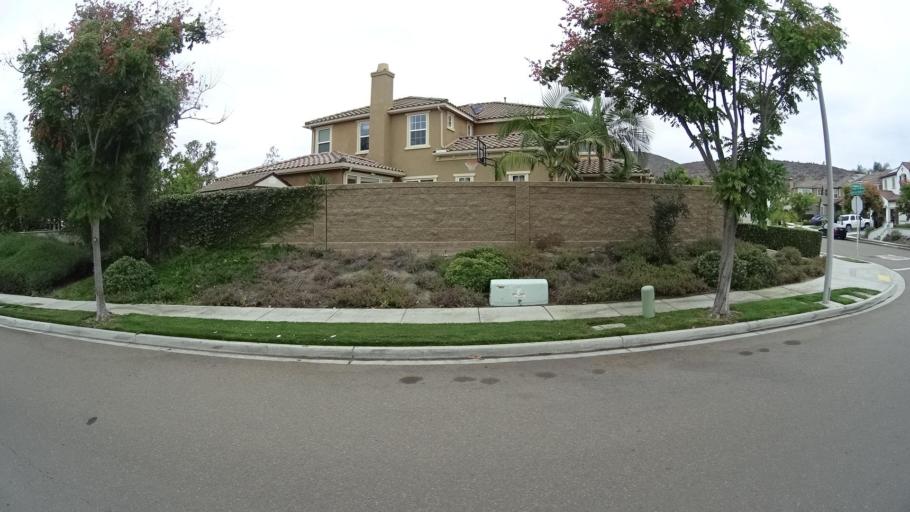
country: US
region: California
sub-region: San Diego County
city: Fairbanks Ranch
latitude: 33.0264
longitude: -117.1178
